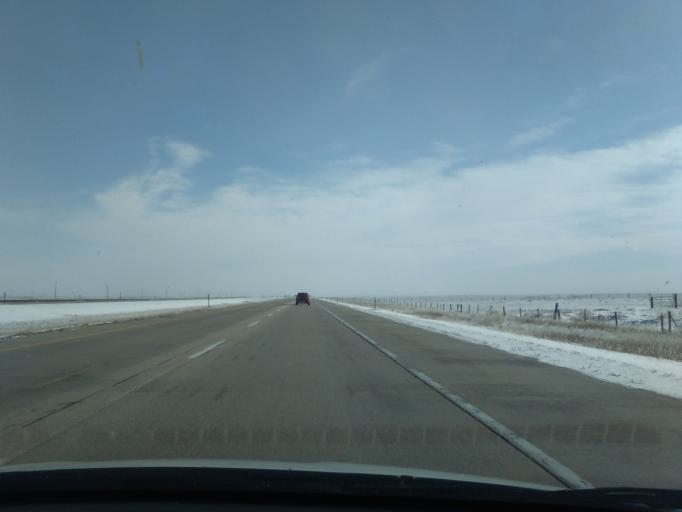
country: US
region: Wyoming
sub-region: Laramie County
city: Pine Bluffs
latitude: 41.1553
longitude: -104.2154
